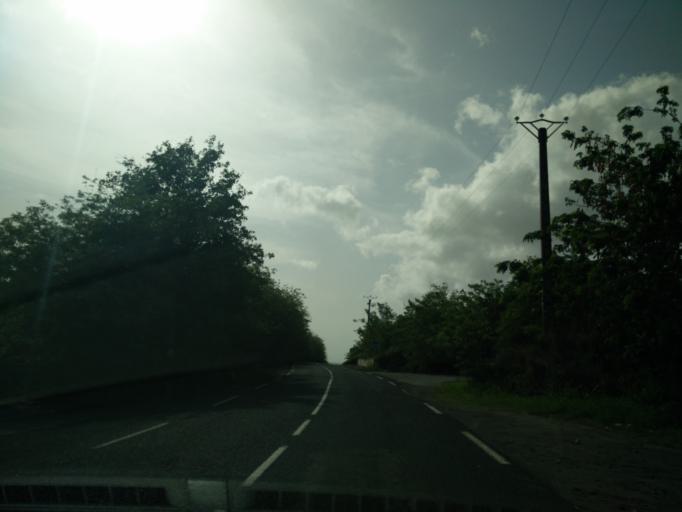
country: MQ
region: Martinique
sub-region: Martinique
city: Saint-Pierre
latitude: 14.7663
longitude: -61.1956
